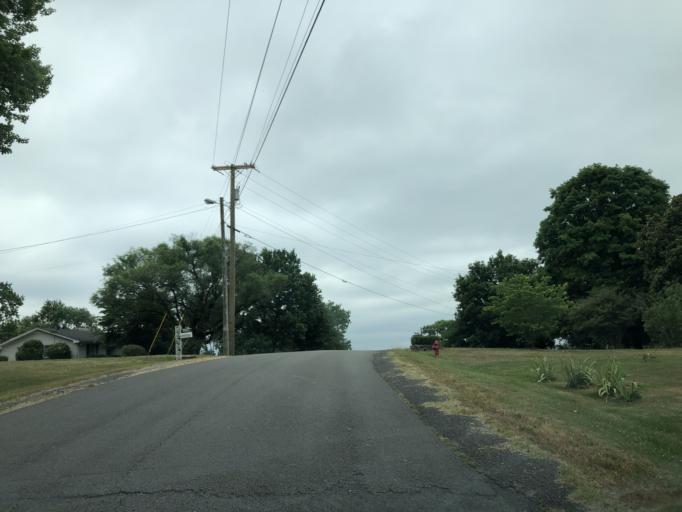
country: US
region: Tennessee
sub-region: Davidson County
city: Goodlettsville
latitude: 36.2778
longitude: -86.7623
